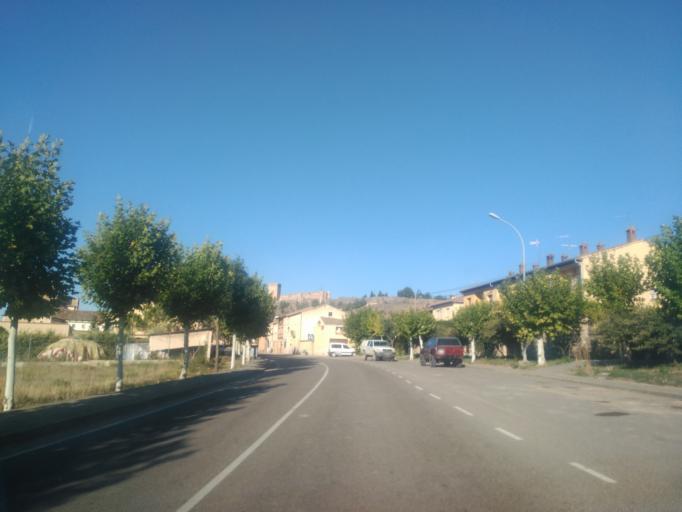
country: ES
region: Castille and Leon
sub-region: Provincia de Burgos
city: Penaranda de Duero
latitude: 41.6898
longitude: -3.4746
